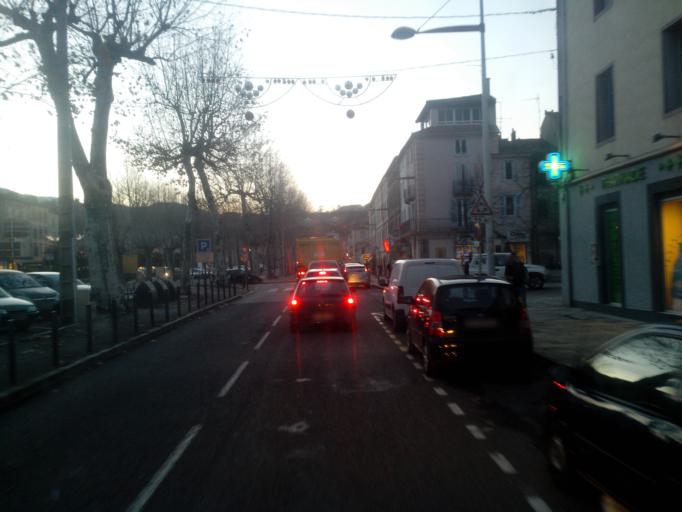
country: FR
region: Midi-Pyrenees
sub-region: Departement de l'Ariege
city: Foix
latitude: 42.9643
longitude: 1.6094
